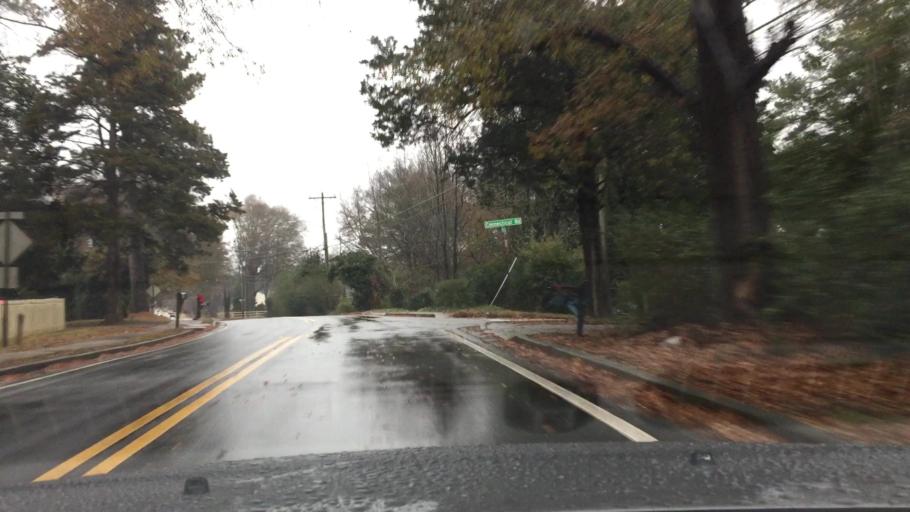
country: US
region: Georgia
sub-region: Cobb County
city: Fair Oaks
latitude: 33.9112
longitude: -84.5749
